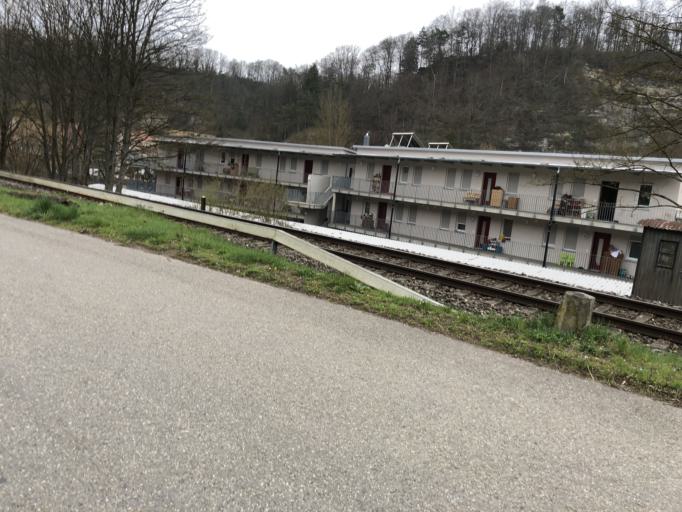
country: DE
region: Baden-Wuerttemberg
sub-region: Tuebingen Region
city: Rottenburg
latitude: 48.4678
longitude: 8.9196
